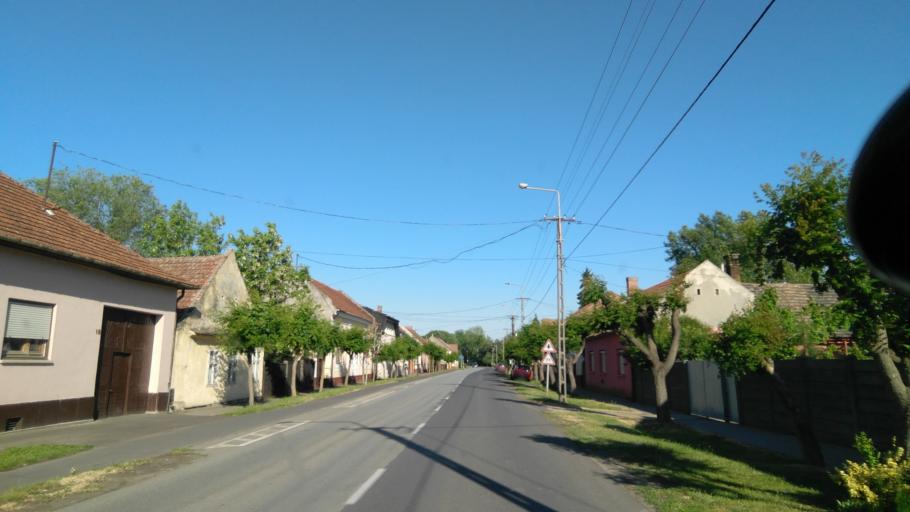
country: HU
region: Bekes
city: Elek
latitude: 46.5305
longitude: 21.2493
